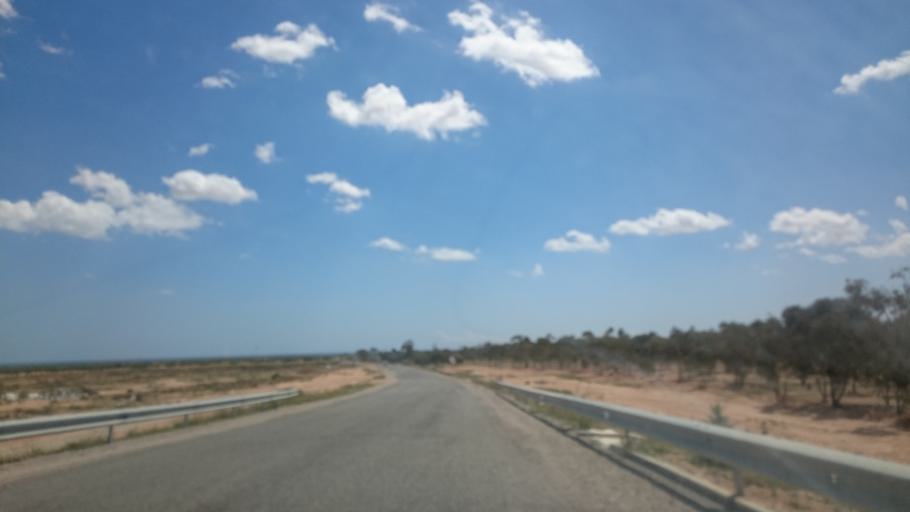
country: TN
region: Safaqis
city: Sfax
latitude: 34.6959
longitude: 10.5589
